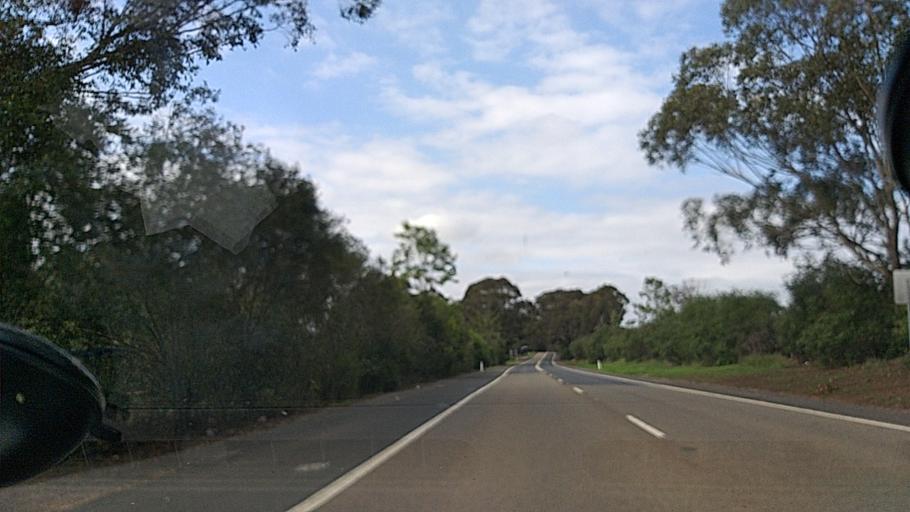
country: AU
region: New South Wales
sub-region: Campbelltown Municipality
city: Glen Alpine
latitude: -34.0826
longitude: 150.7772
